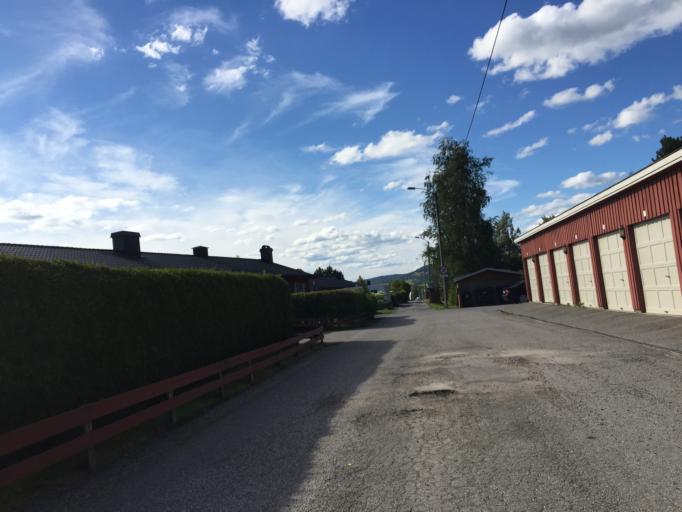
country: NO
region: Hedmark
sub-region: Kongsvinger
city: Kongsvinger
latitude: 60.1992
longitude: 11.9852
